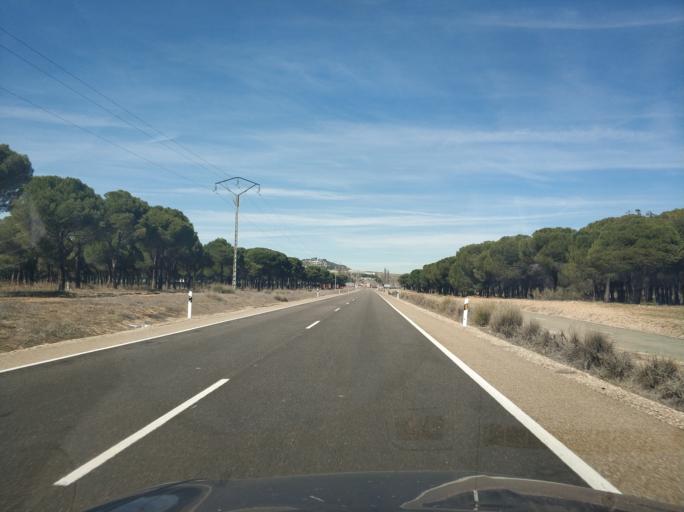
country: ES
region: Castille and Leon
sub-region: Provincia de Valladolid
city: Simancas
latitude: 41.5773
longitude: -4.8115
